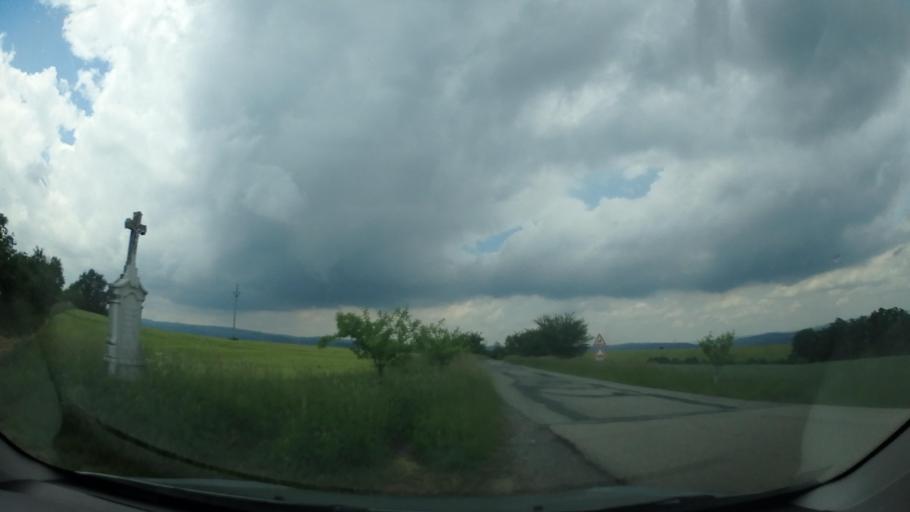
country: CZ
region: South Moravian
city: Boritov
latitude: 49.4559
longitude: 16.5983
